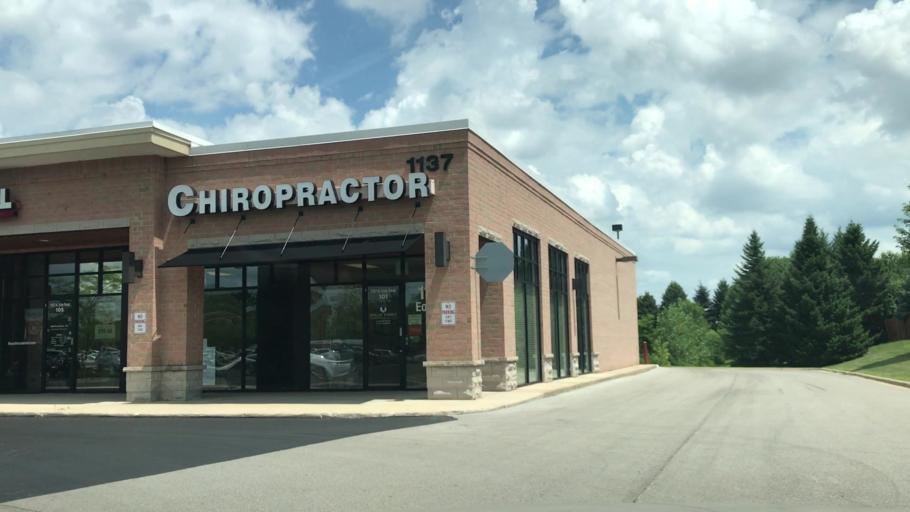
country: US
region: Illinois
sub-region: DuPage County
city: Warrenville
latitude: 41.7790
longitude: -88.2387
